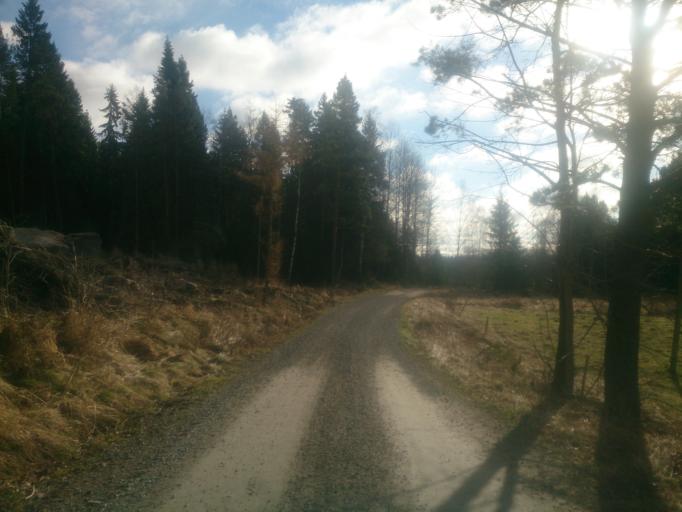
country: SE
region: OEstergoetland
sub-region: Atvidabergs Kommun
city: Atvidaberg
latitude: 58.2344
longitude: 16.1670
